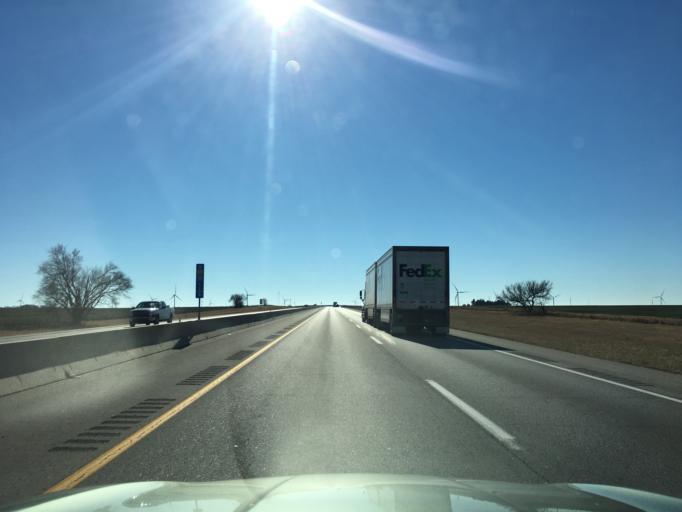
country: US
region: Kansas
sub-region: Sumner County
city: Wellington
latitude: 37.1672
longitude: -97.3395
